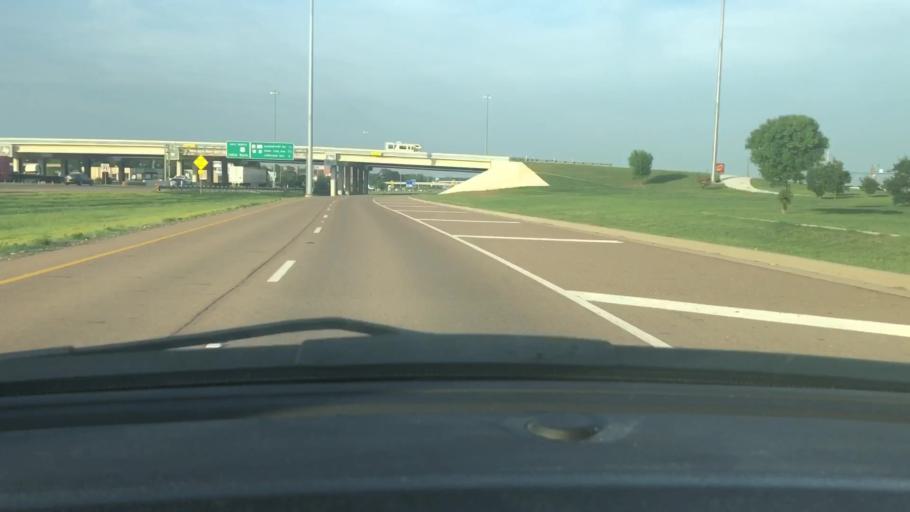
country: US
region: Texas
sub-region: Bowie County
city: Wake Village
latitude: 33.4552
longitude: -94.0881
